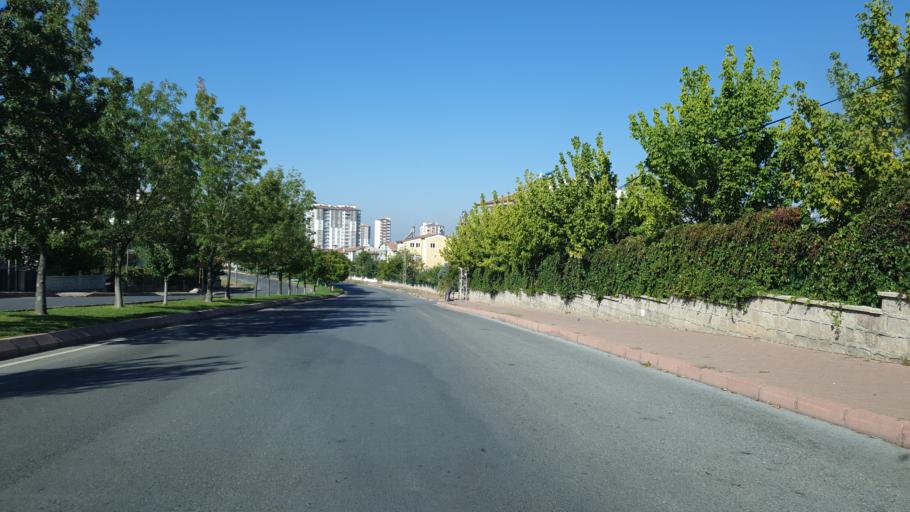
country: TR
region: Kayseri
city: Kocasinan
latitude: 38.7774
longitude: 35.5852
